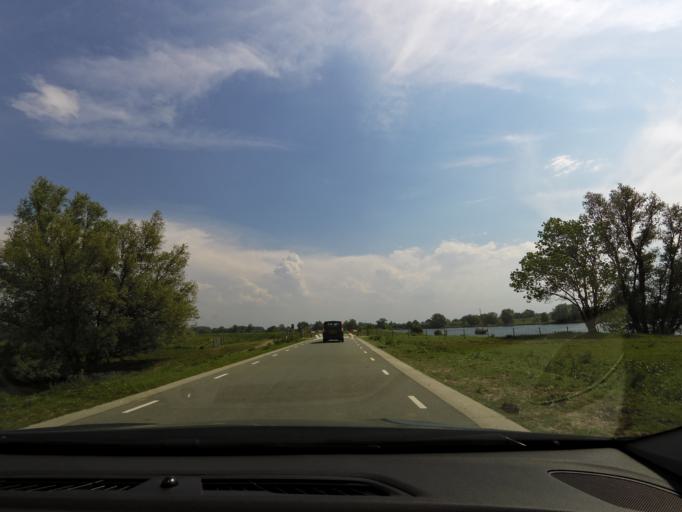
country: NL
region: North Brabant
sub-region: Gemeente Woudrichem
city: Woudrichem
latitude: 51.8064
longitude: 5.0251
